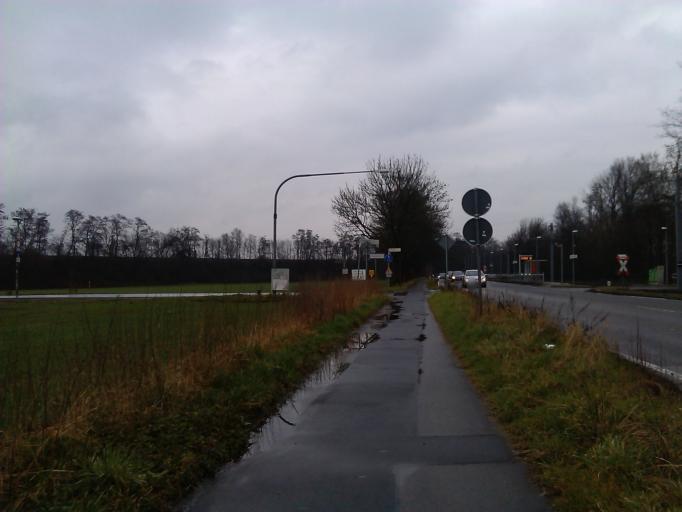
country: DE
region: North Rhine-Westphalia
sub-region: Regierungsbezirk Dusseldorf
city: Ratingen
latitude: 51.2813
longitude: 6.8358
